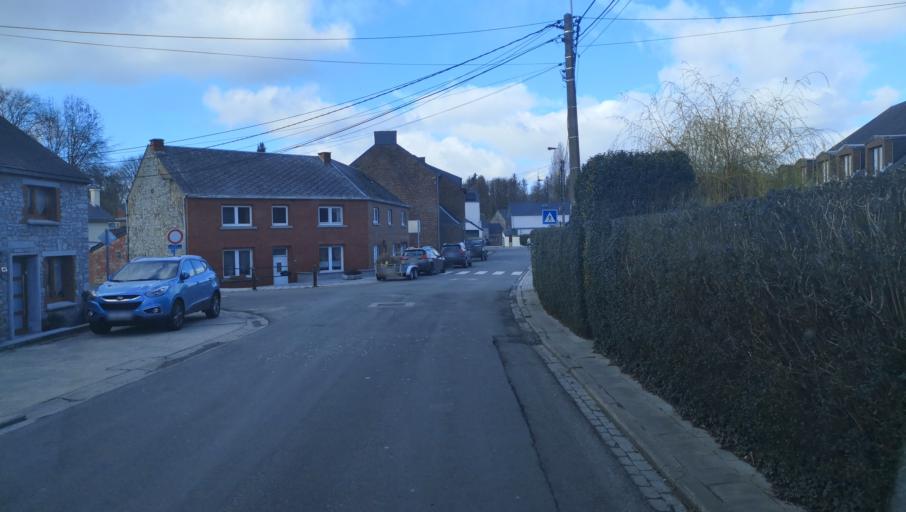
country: BE
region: Wallonia
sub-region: Province de Namur
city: Namur
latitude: 50.5016
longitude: 4.8722
